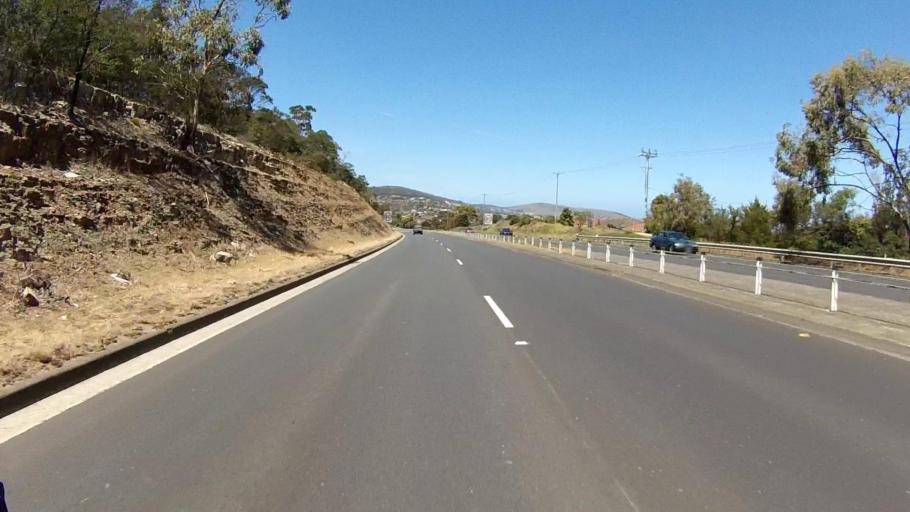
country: AU
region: Tasmania
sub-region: Clarence
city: Howrah
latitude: -42.8711
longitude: 147.3996
